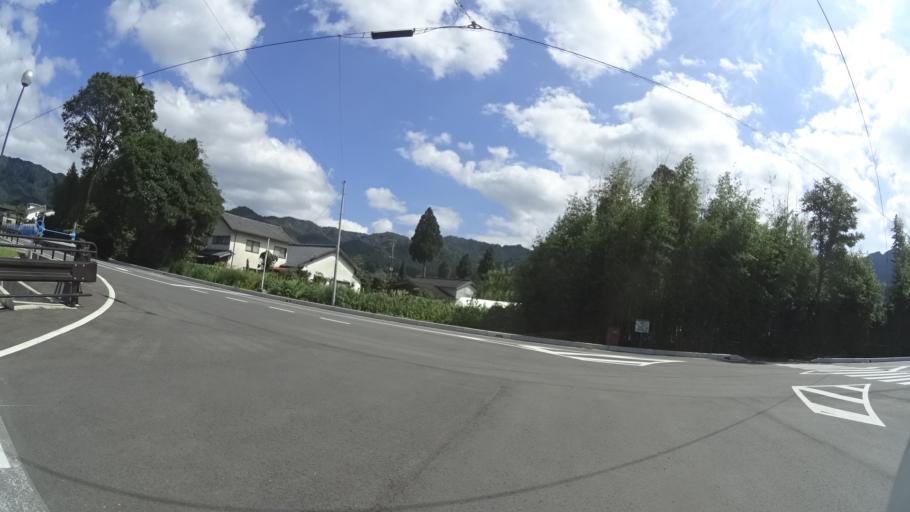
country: JP
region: Kumamoto
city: Aso
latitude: 32.8128
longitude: 131.1172
